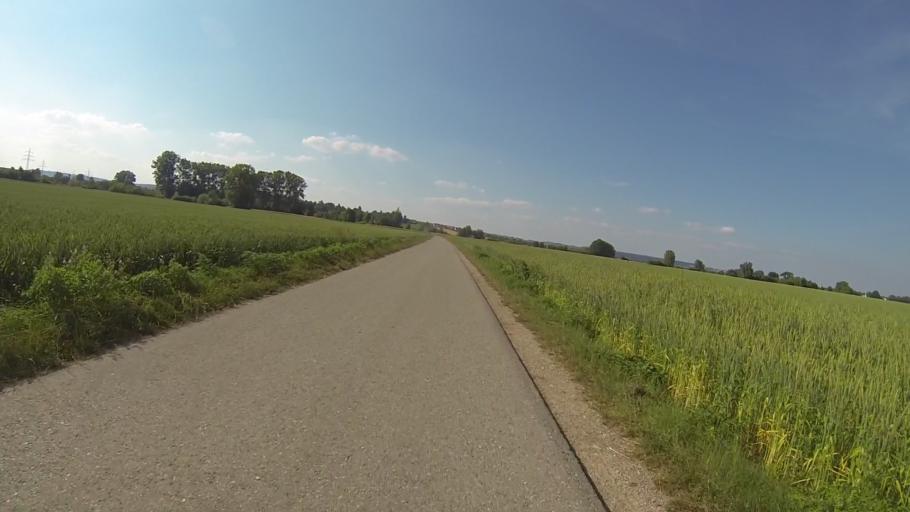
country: DE
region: Bavaria
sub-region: Swabia
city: Neu-Ulm
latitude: 48.3957
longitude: 10.0504
